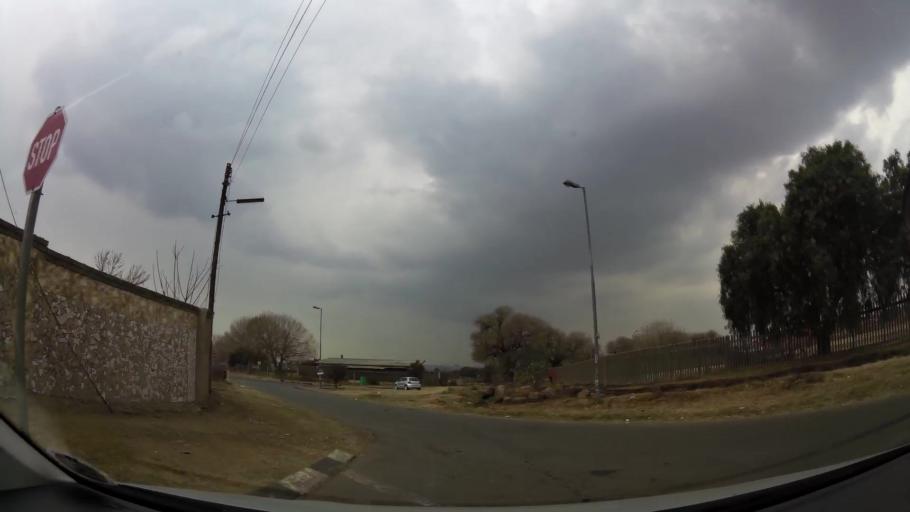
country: ZA
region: Gauteng
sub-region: City of Johannesburg Metropolitan Municipality
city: Soweto
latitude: -26.2628
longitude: 27.8684
